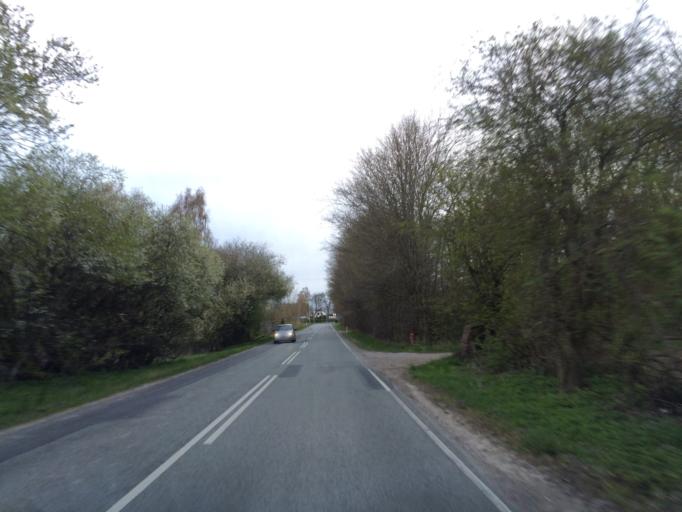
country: DK
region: South Denmark
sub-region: Odense Kommune
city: Bellinge
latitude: 55.3719
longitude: 10.2661
